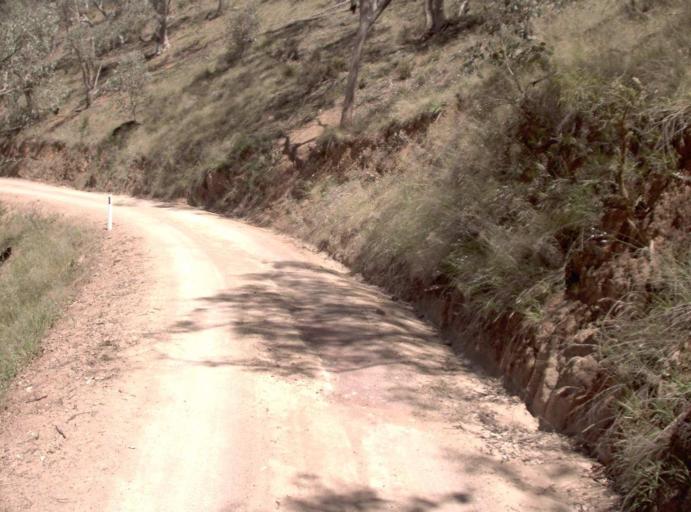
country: AU
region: New South Wales
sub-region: Snowy River
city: Jindabyne
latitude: -37.0877
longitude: 148.3623
